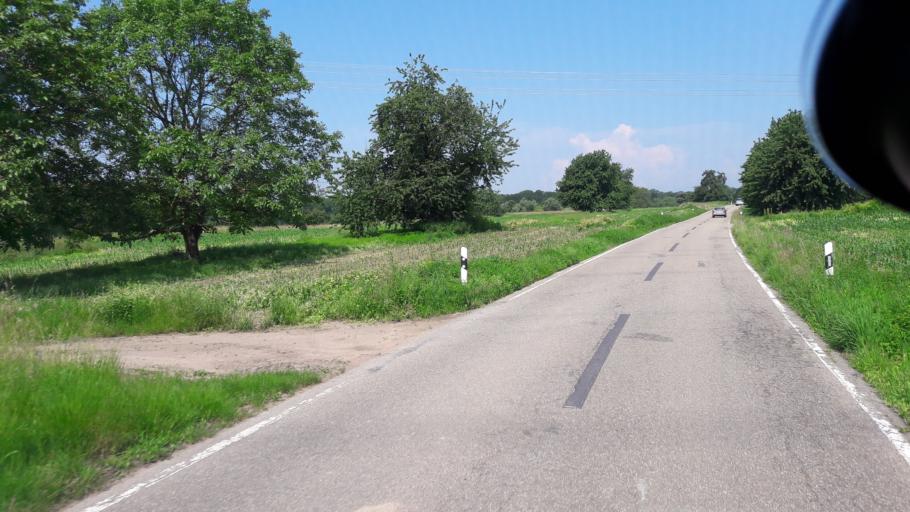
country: DE
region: Baden-Wuerttemberg
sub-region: Karlsruhe Region
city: Kuppenheim
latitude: 48.8489
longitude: 8.2494
